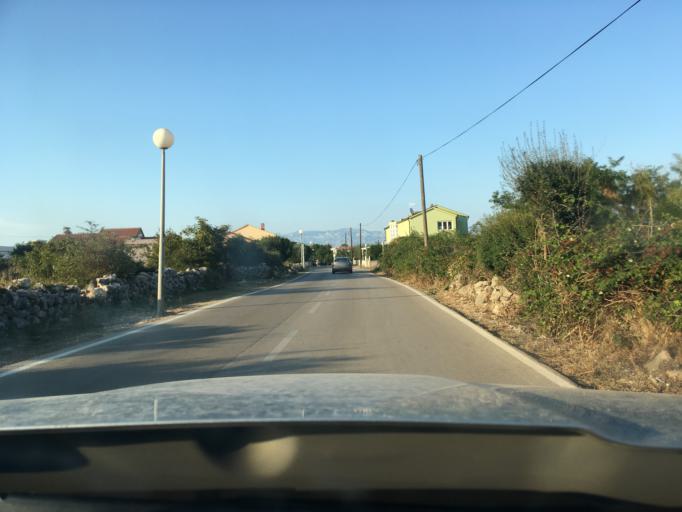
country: HR
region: Zadarska
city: Vir
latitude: 44.2970
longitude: 15.0760
